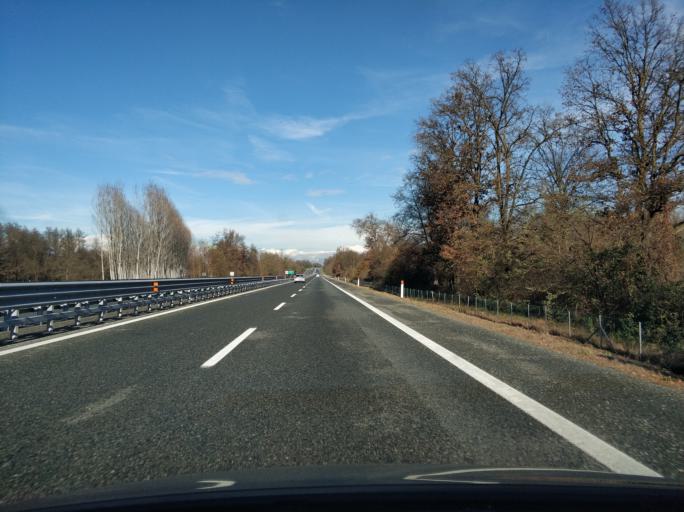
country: IT
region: Piedmont
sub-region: Provincia di Torino
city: Foglizzo
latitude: 45.2910
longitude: 7.8155
